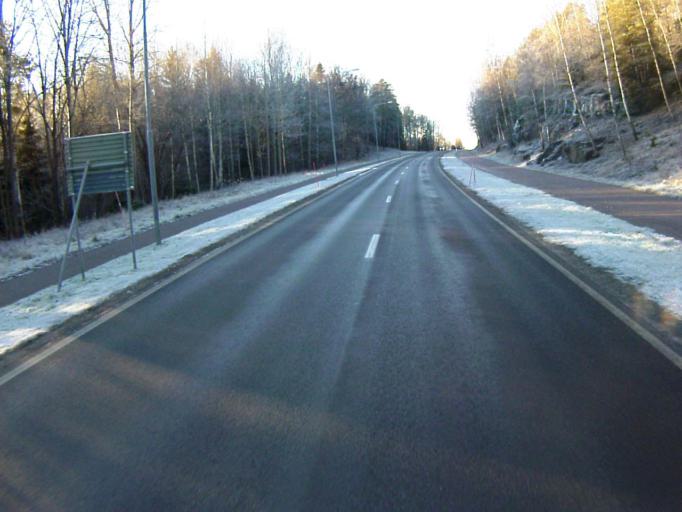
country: SE
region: Soedermanland
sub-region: Eskilstuna Kommun
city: Skogstorp
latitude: 59.3379
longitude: 16.4820
